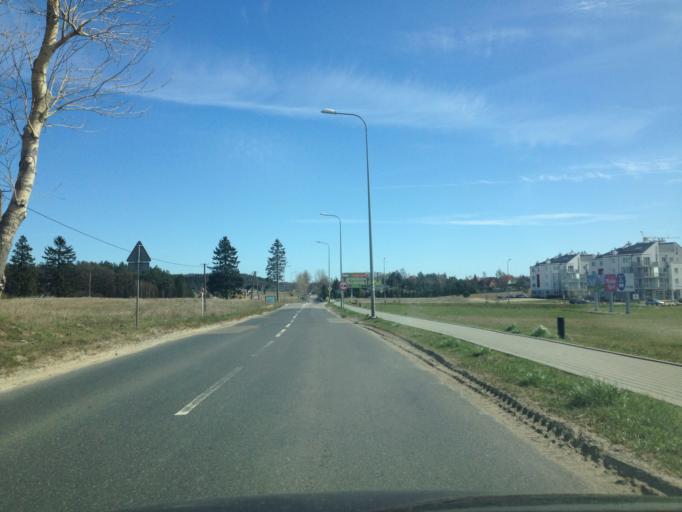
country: PL
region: Pomeranian Voivodeship
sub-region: Powiat kartuski
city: Chwaszczyno
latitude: 54.4885
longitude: 18.4270
